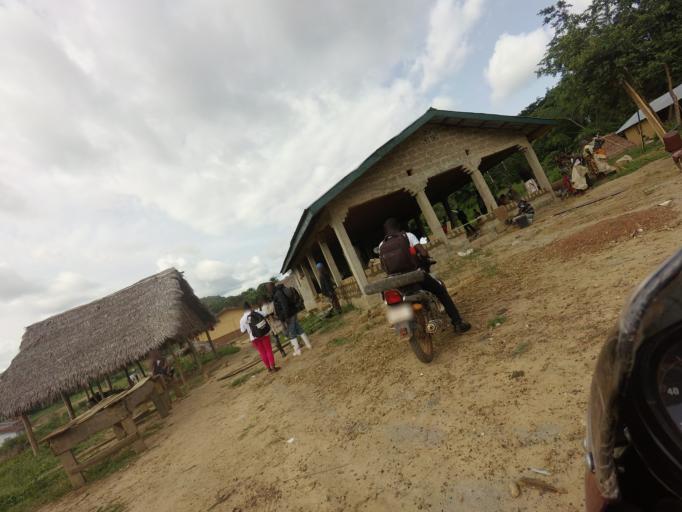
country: SL
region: Eastern Province
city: Jojoima
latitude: 7.7785
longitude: -10.8126
